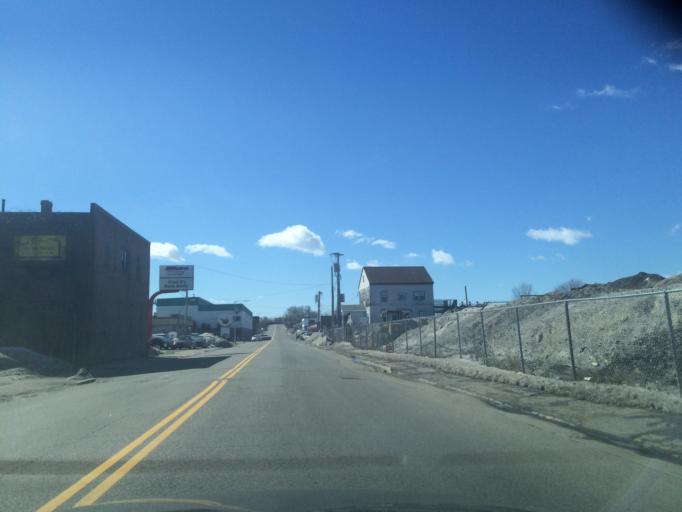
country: US
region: Massachusetts
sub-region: Norfolk County
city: Dedham
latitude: 42.2444
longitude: -71.1297
